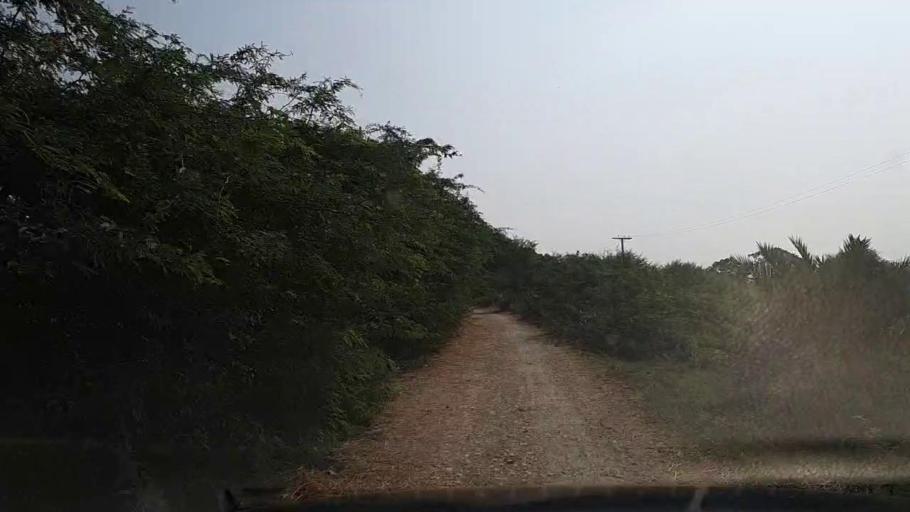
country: PK
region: Sindh
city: Mirpur Batoro
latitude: 24.6925
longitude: 68.2196
